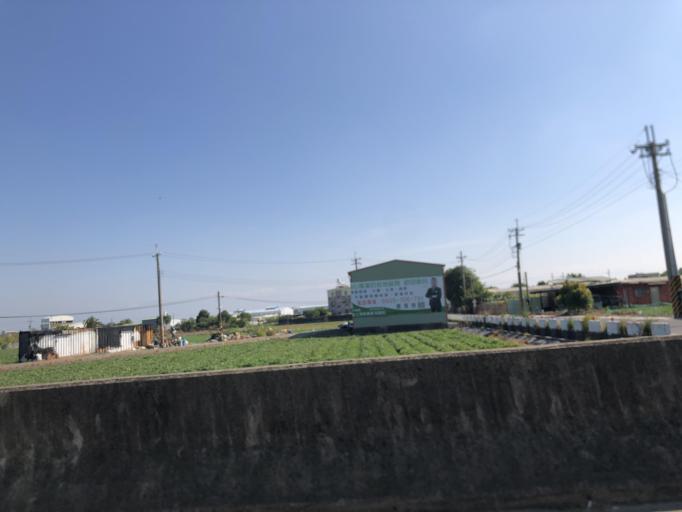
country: TW
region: Taiwan
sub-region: Tainan
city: Tainan
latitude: 23.0196
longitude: 120.2892
